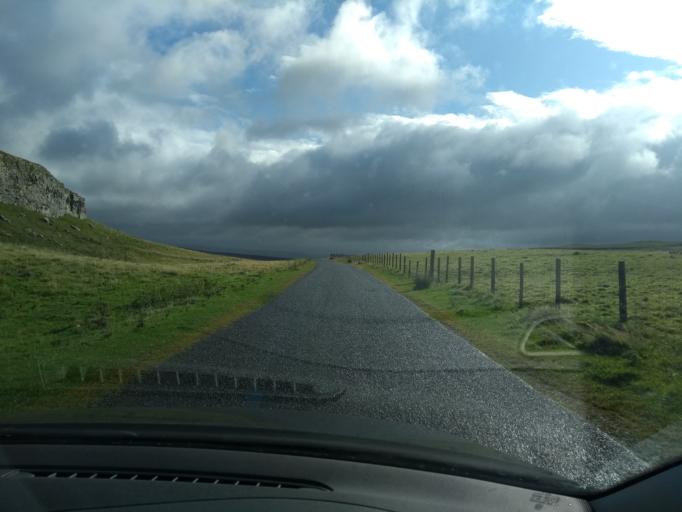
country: GB
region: England
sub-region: North Yorkshire
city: Settle
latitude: 54.0826
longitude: -2.1767
